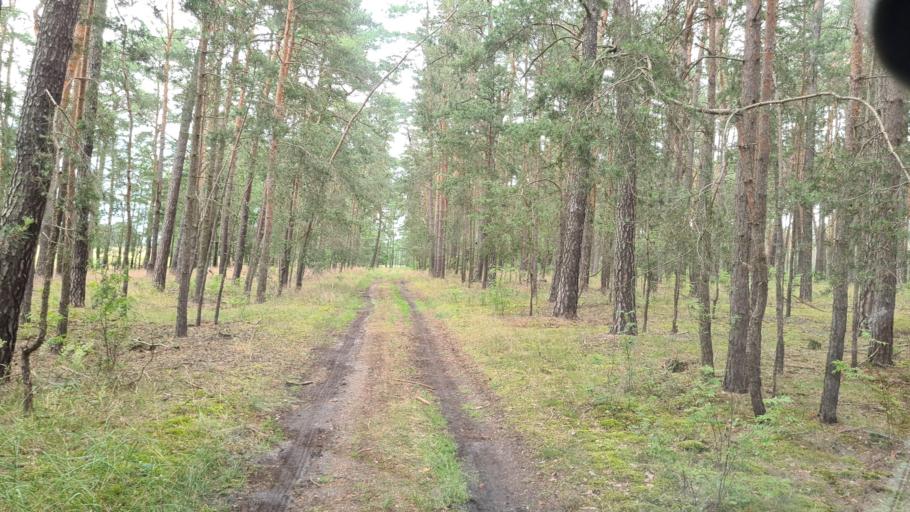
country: DE
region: Brandenburg
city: Crinitz
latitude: 51.7149
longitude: 13.8312
